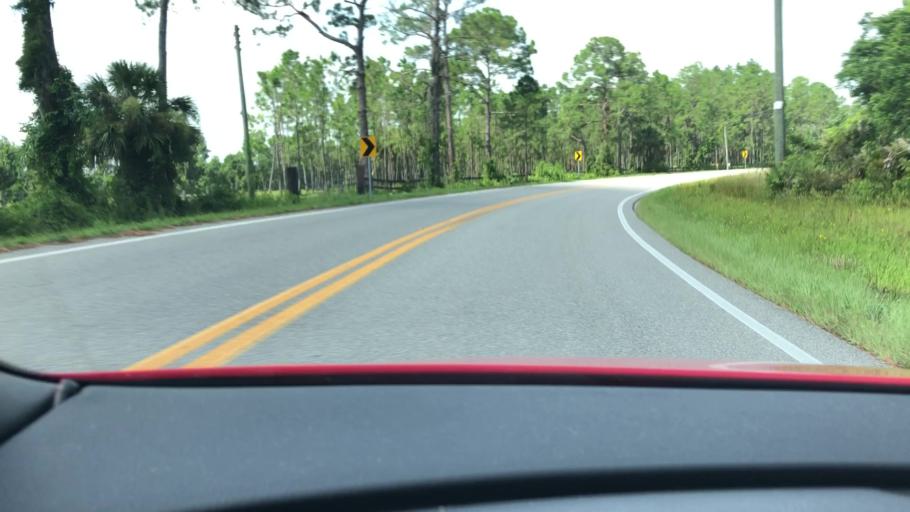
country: US
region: Florida
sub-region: Volusia County
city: Samsula-Spruce Creek
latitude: 29.0273
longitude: -81.0976
